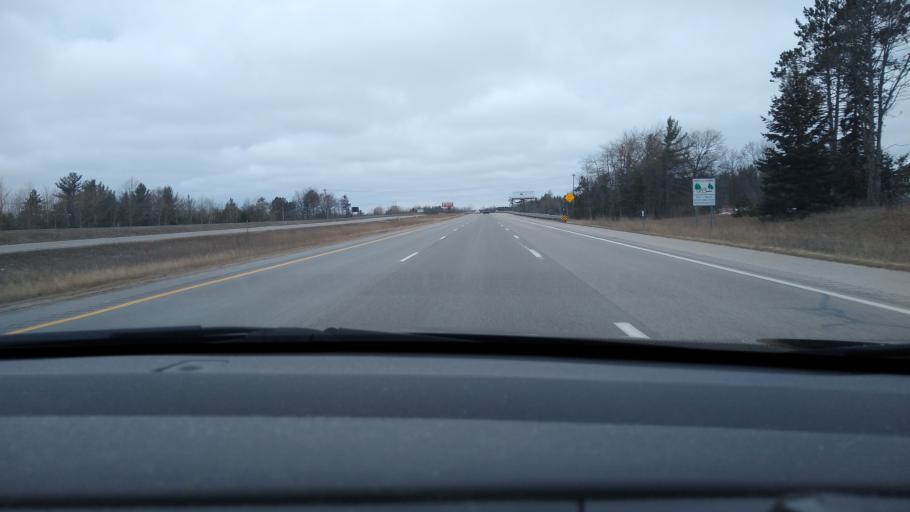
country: US
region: Michigan
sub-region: Otsego County
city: Gaylord
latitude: 44.9883
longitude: -84.6777
